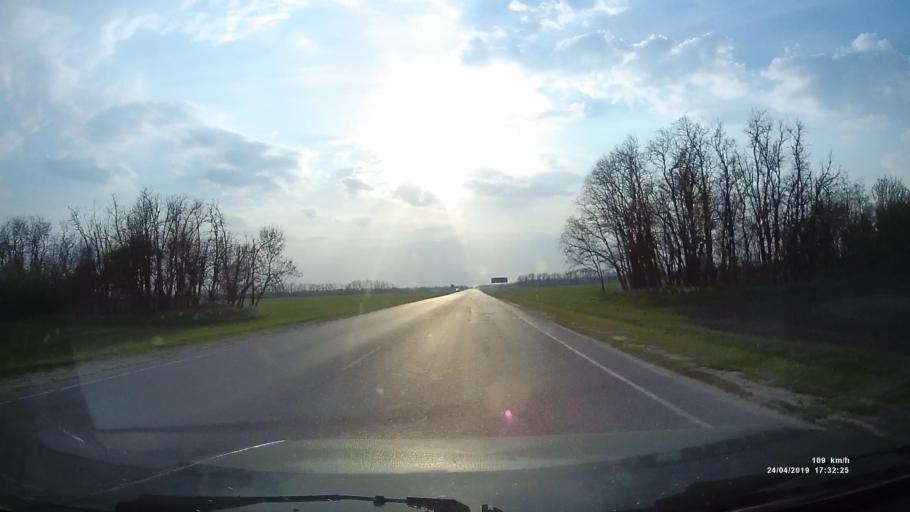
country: RU
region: Rostov
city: Tselina
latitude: 46.5257
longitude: 41.0964
